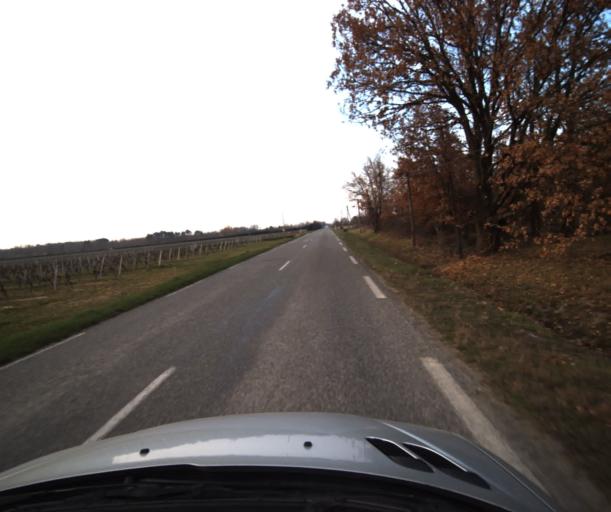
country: FR
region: Midi-Pyrenees
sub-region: Departement de la Haute-Garonne
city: Fronton
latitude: 43.8583
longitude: 1.3842
